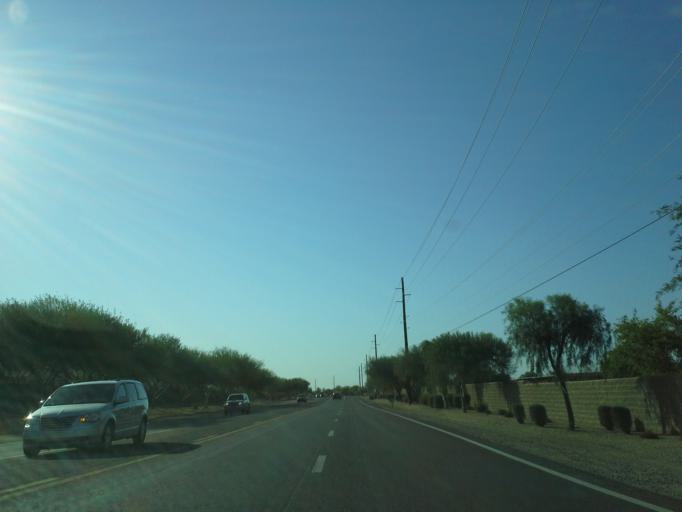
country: US
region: Arizona
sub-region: Pinal County
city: San Tan Valley
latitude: 33.1655
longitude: -111.5668
